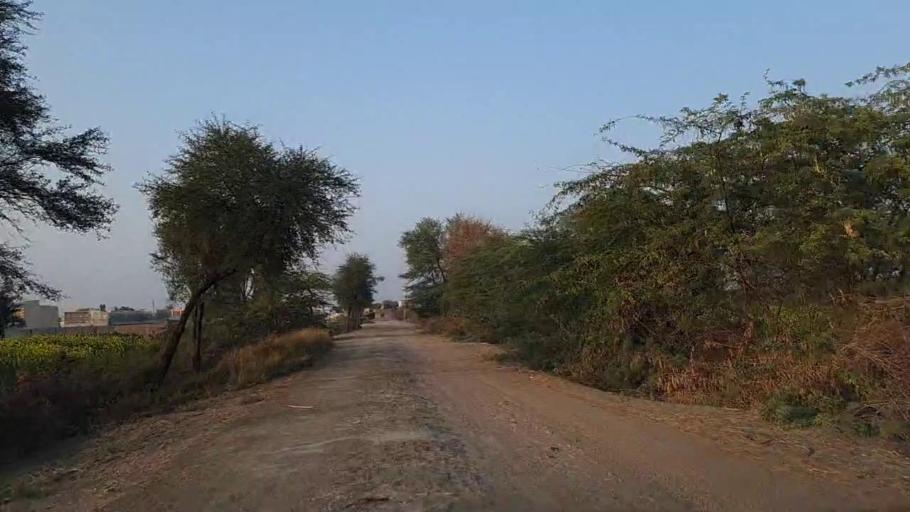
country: PK
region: Sindh
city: Daur
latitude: 26.4332
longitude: 68.3873
